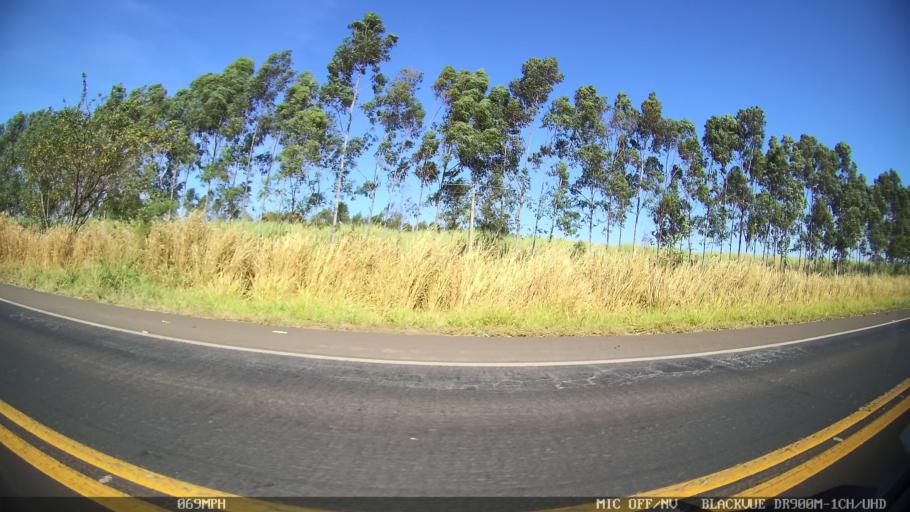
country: BR
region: Sao Paulo
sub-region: Olimpia
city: Olimpia
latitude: -20.6225
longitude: -48.7711
